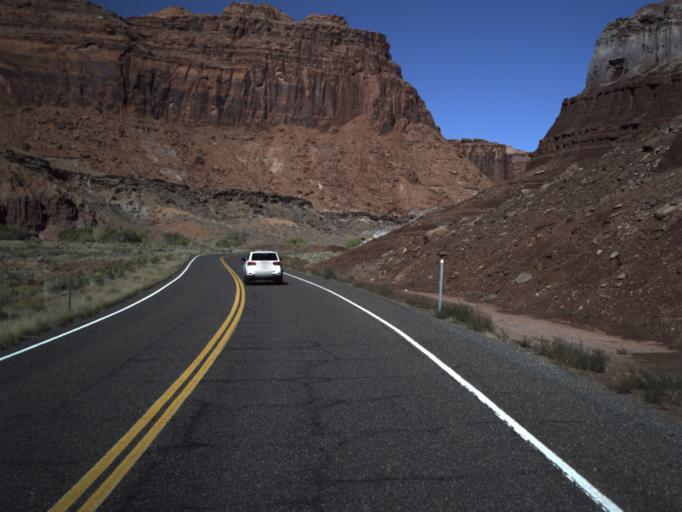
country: US
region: Utah
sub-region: San Juan County
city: Blanding
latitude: 37.9047
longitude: -110.4521
